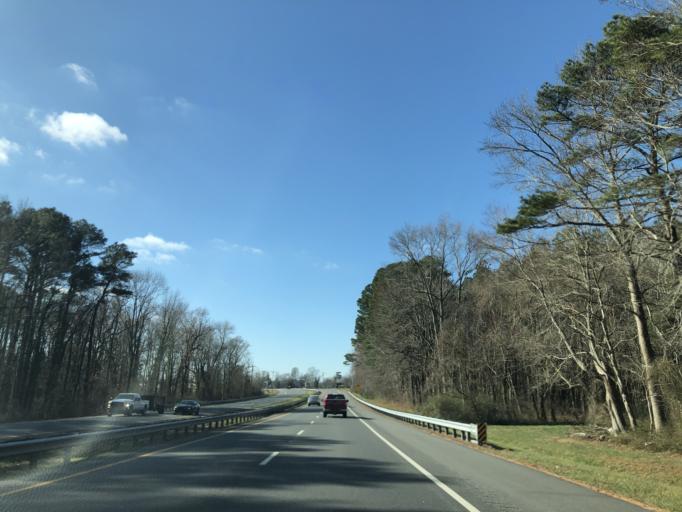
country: US
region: Maryland
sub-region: Worcester County
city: Berlin
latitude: 38.3180
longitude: -75.2155
